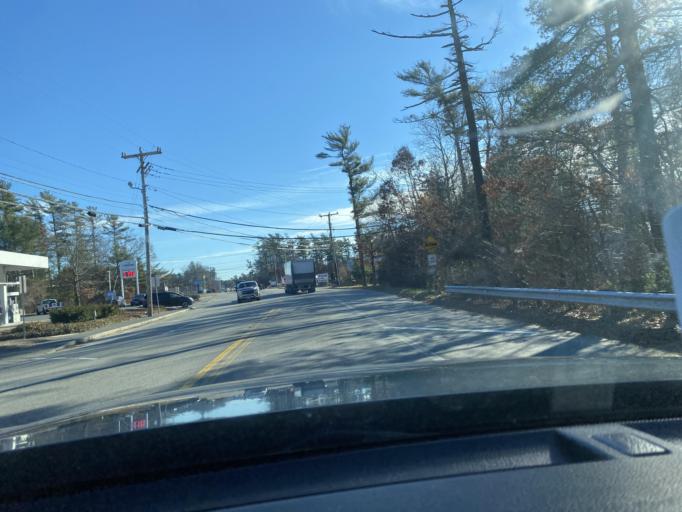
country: US
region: Massachusetts
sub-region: Plymouth County
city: West Wareham
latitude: 41.7885
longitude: -70.7508
